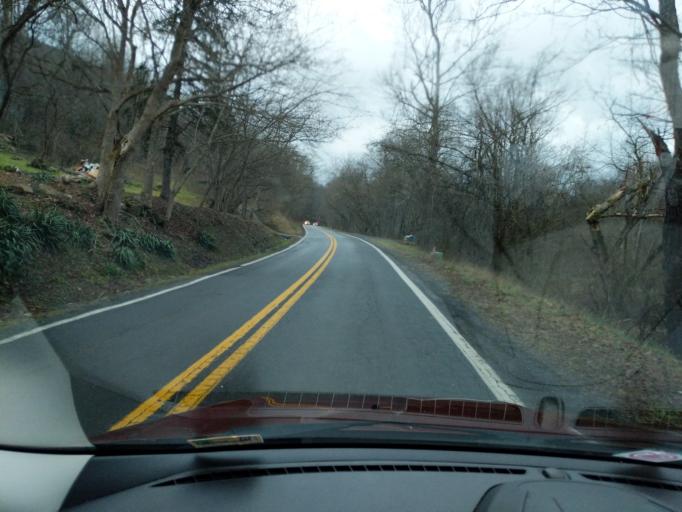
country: US
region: West Virginia
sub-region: Greenbrier County
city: Alderson
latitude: 37.7399
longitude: -80.6239
